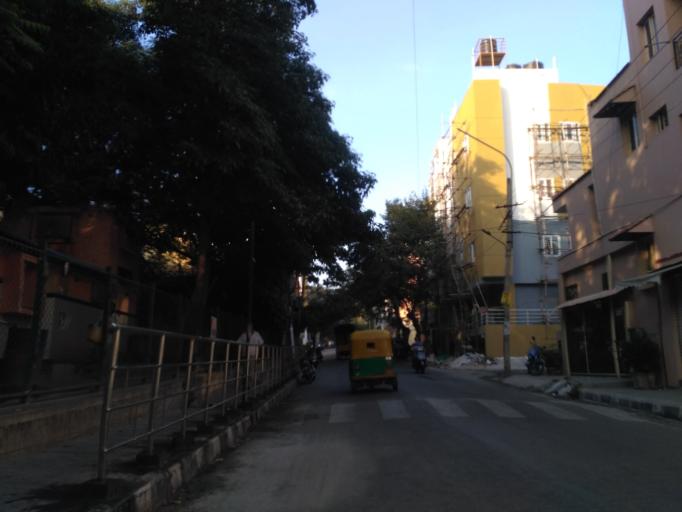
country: IN
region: Karnataka
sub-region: Bangalore Urban
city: Bangalore
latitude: 12.9634
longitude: 77.5378
